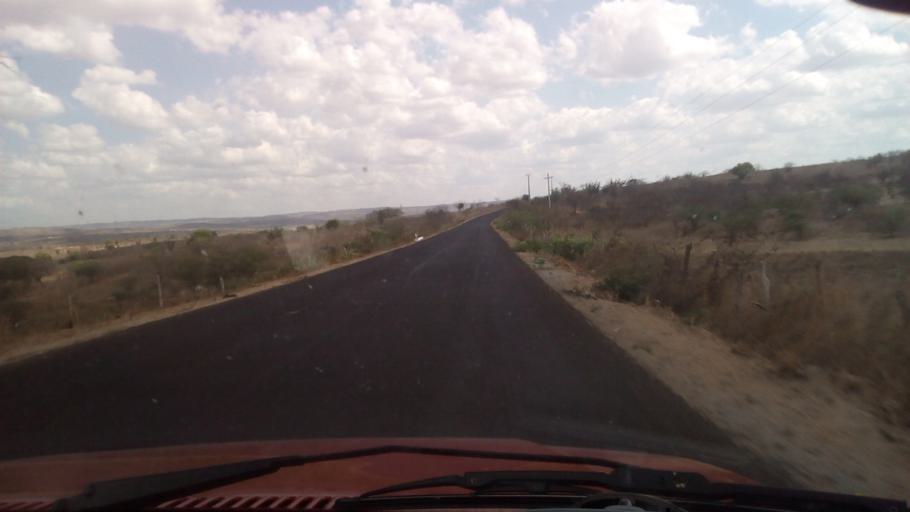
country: BR
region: Paraiba
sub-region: Cacimba De Dentro
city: Cacimba de Dentro
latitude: -6.6623
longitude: -35.7596
